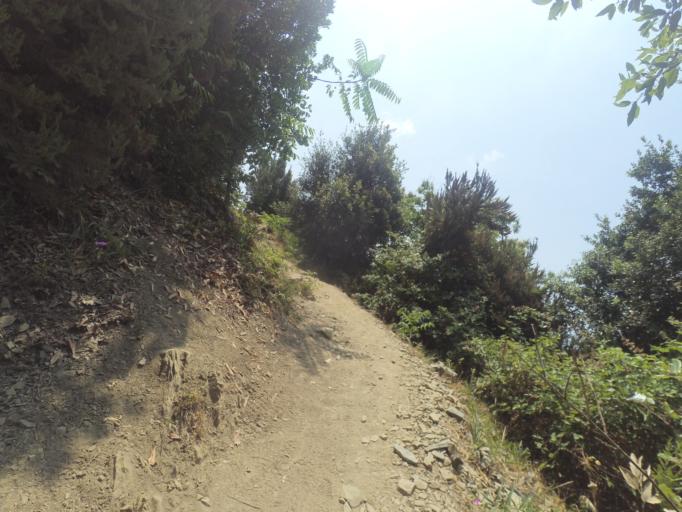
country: IT
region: Liguria
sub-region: Provincia di La Spezia
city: Riomaggiore
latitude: 44.1244
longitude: 9.7155
